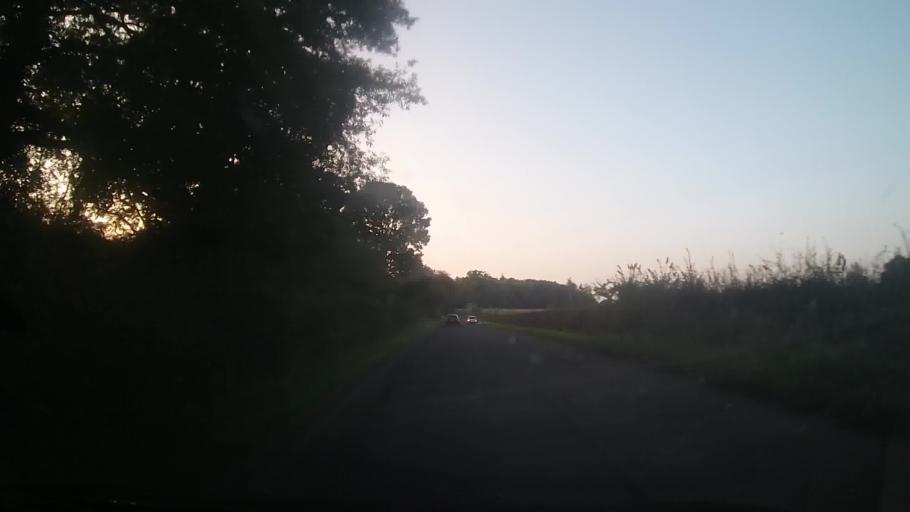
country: GB
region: England
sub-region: Shropshire
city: Bicton
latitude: 52.7652
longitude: -2.7998
